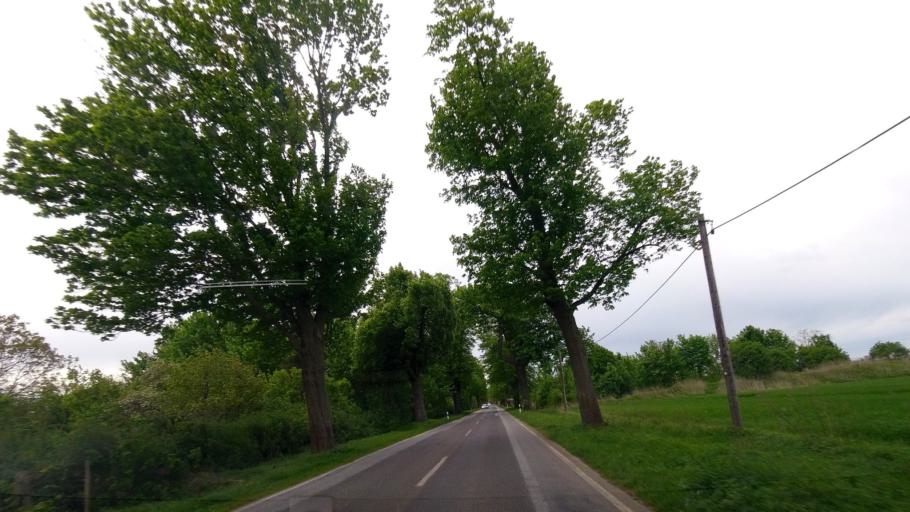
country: DE
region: Brandenburg
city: Dahme
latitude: 51.8780
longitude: 13.4204
